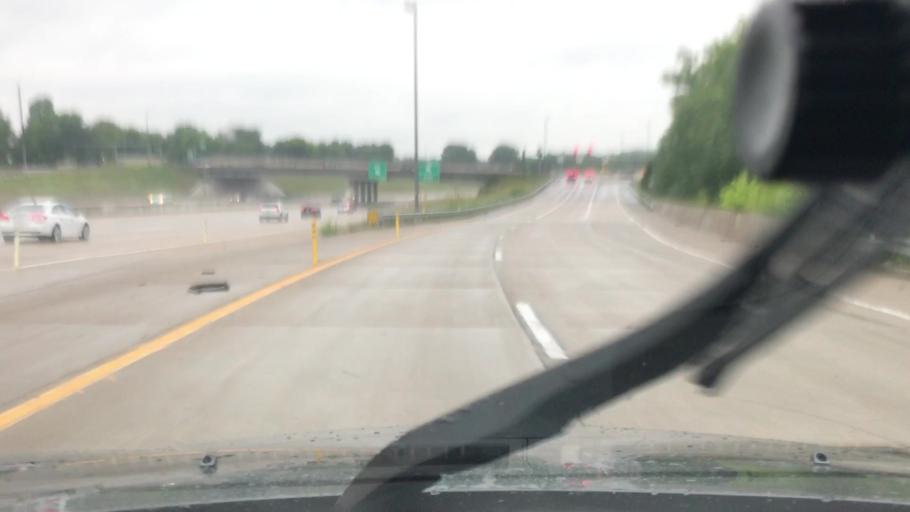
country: US
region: Missouri
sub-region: Saint Louis County
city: Maryland Heights
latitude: 38.6964
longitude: -90.4625
